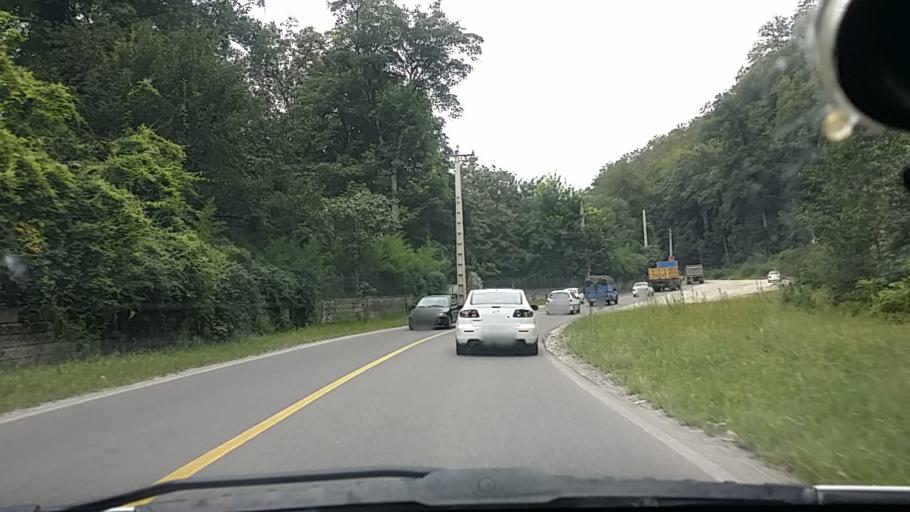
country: IR
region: Mazandaran
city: Chalus
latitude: 36.6082
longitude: 51.3866
